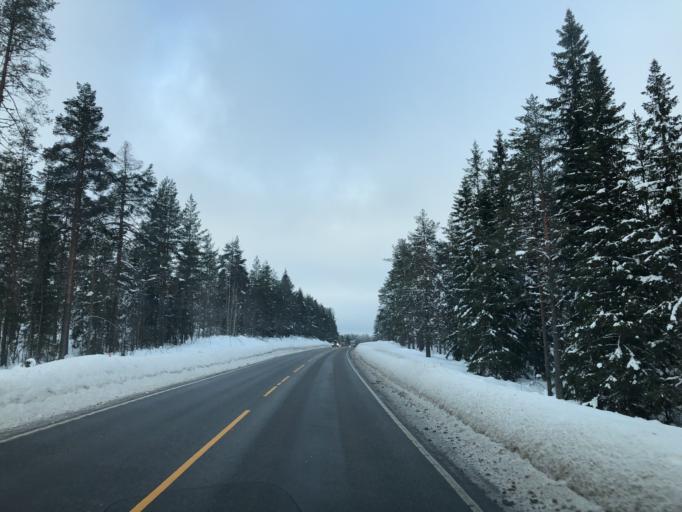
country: NO
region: Hedmark
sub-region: Trysil
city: Innbygda
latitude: 61.2253
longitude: 12.2467
